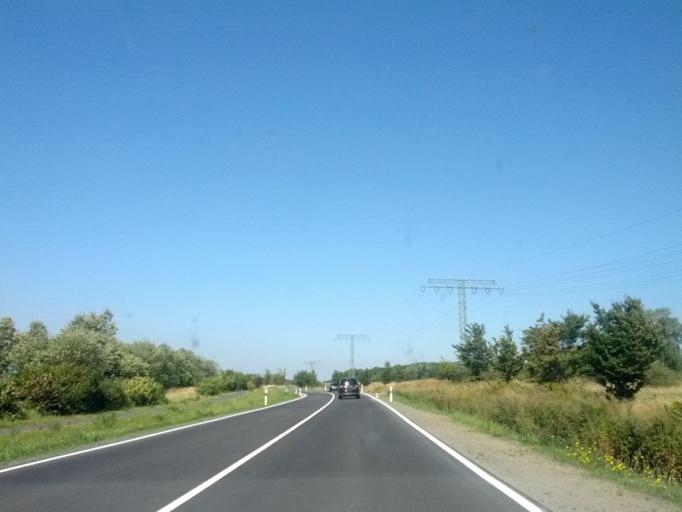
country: DE
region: Mecklenburg-Vorpommern
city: Sagard
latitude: 54.4947
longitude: 13.5743
